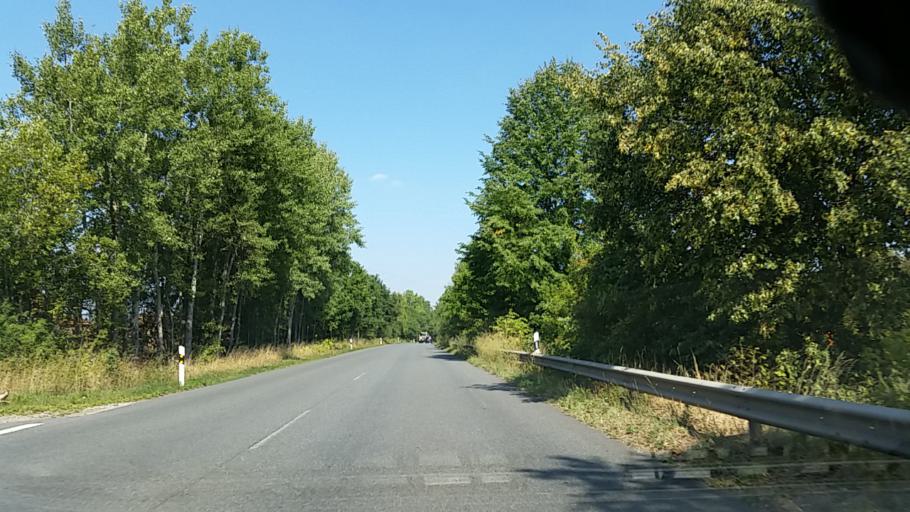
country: DE
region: Lower Saxony
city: Emmendorf
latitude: 52.9934
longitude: 10.5682
